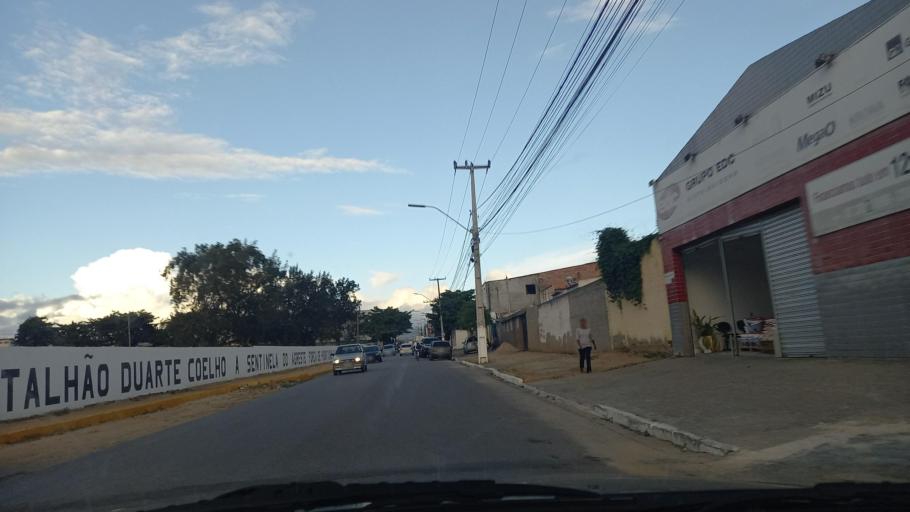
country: BR
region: Pernambuco
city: Garanhuns
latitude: -8.8840
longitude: -36.4714
